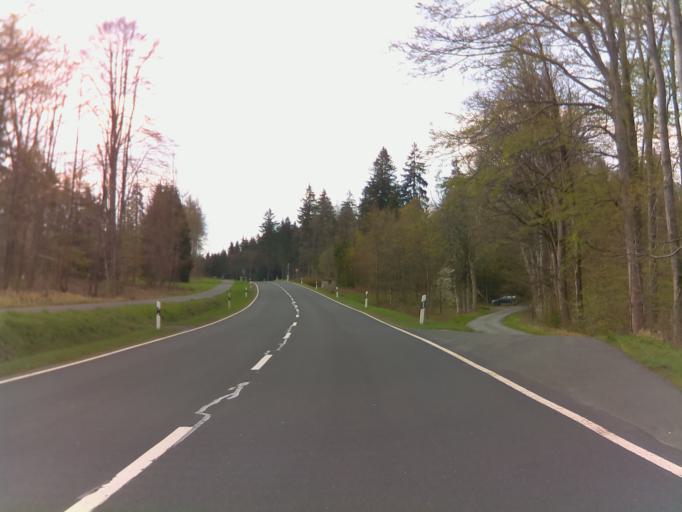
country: DE
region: Bavaria
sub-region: Upper Franconia
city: Ludwigsstadt
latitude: 50.4560
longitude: 11.3484
